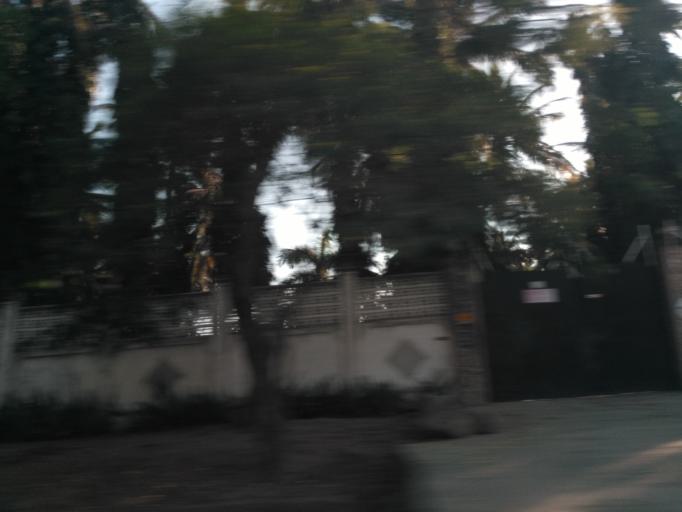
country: TZ
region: Dar es Salaam
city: Magomeni
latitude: -6.7545
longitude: 39.2453
